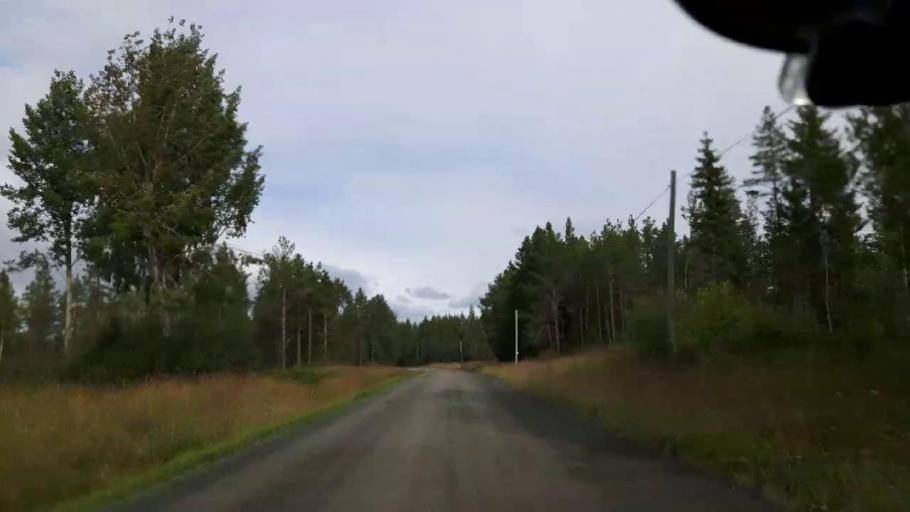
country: SE
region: Jaemtland
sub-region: Krokoms Kommun
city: Krokom
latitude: 63.3724
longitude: 14.1293
